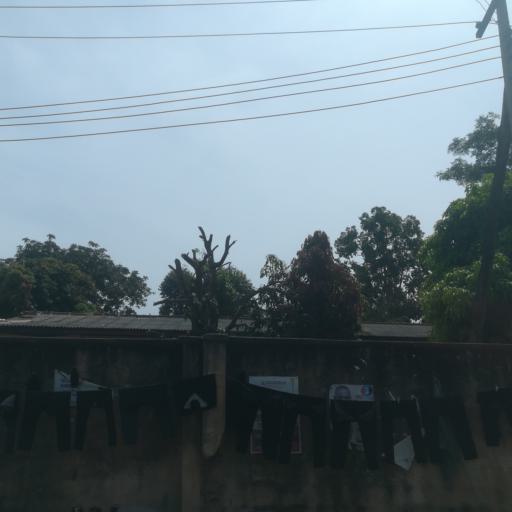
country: NG
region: Plateau
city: Jos
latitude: 9.9054
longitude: 8.8736
